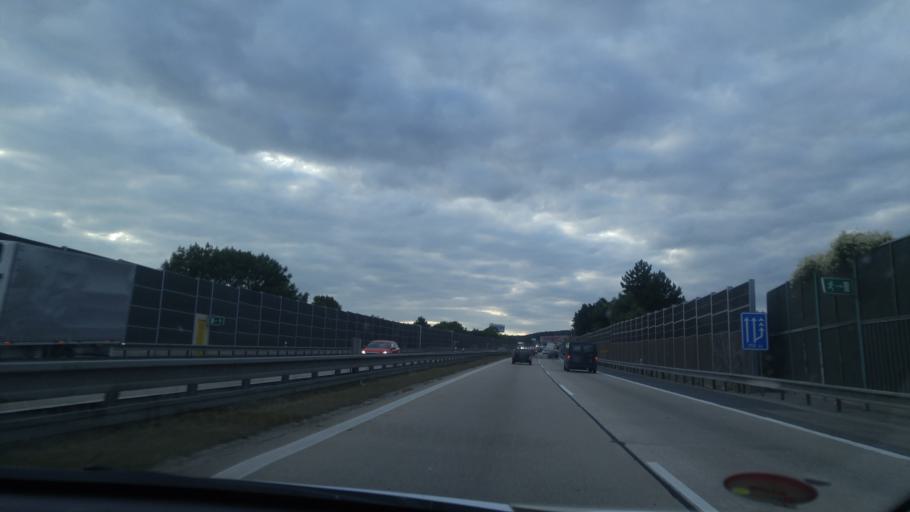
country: CZ
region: South Moravian
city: Troubsko
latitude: 49.1777
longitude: 16.4933
